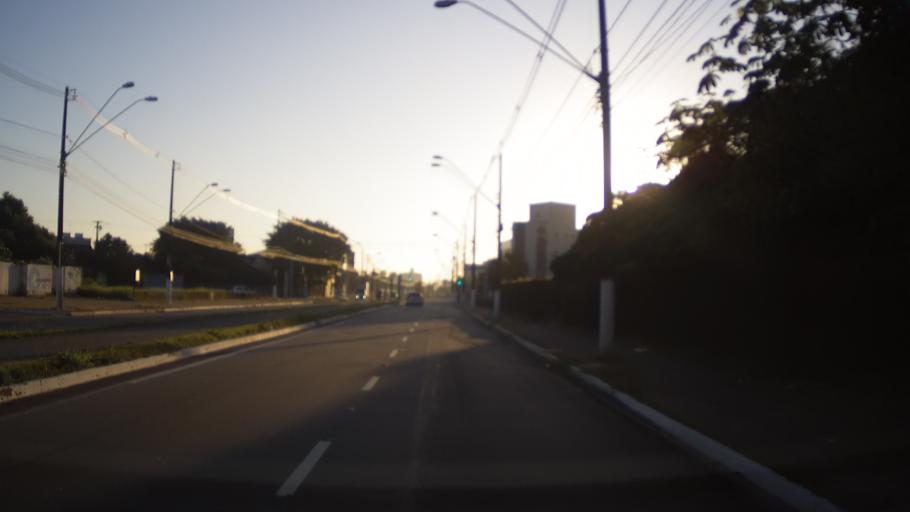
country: BR
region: Sao Paulo
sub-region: Praia Grande
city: Praia Grande
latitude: -24.0333
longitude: -46.4990
